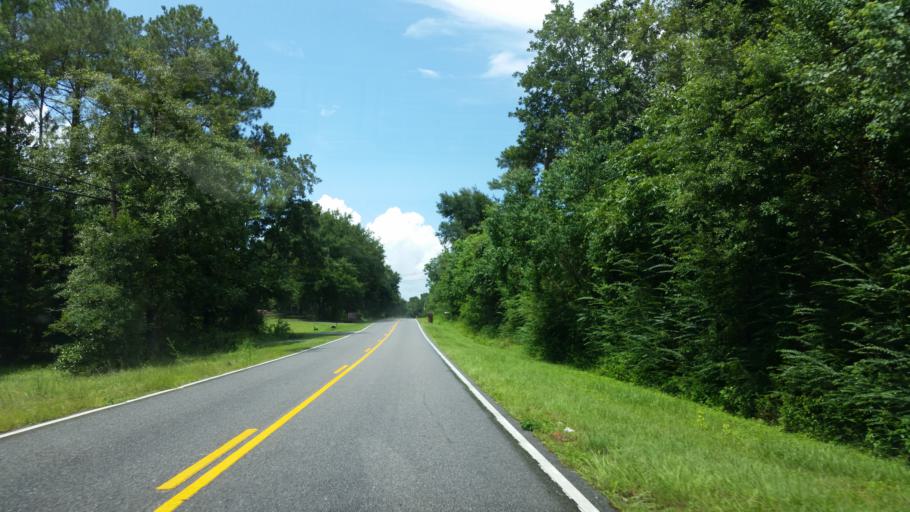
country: US
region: Florida
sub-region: Escambia County
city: Gonzalez
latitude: 30.5588
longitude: -87.2996
